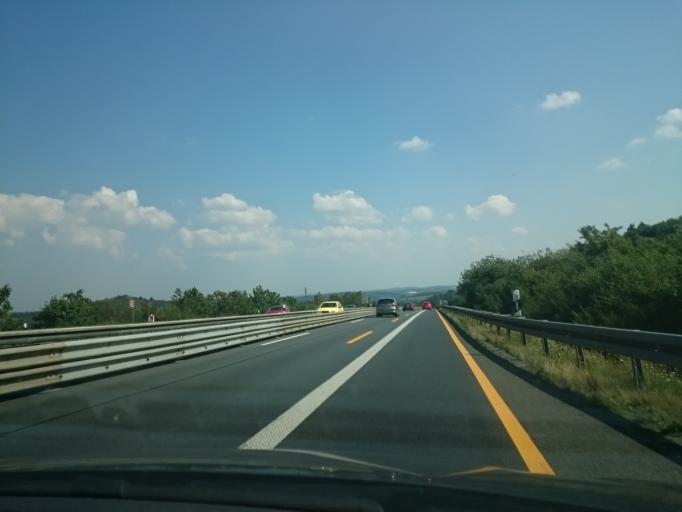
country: DE
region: Saxony
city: Weischlitz
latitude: 50.4051
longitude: 12.0229
